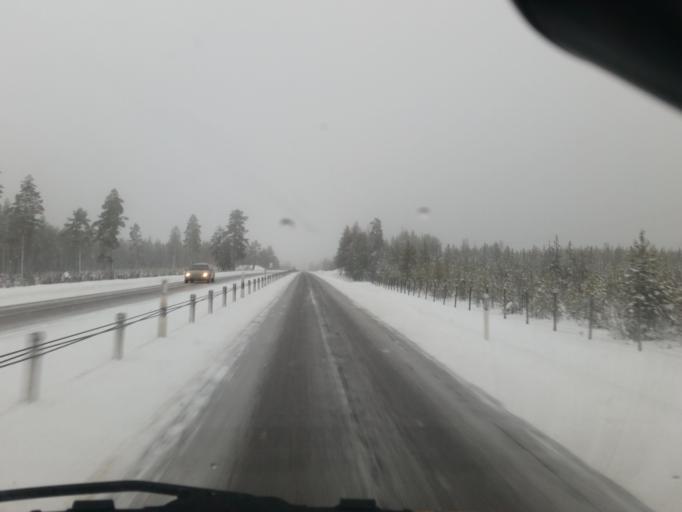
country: SE
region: Norrbotten
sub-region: Pitea Kommun
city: Pitea
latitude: 65.1825
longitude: 21.5052
